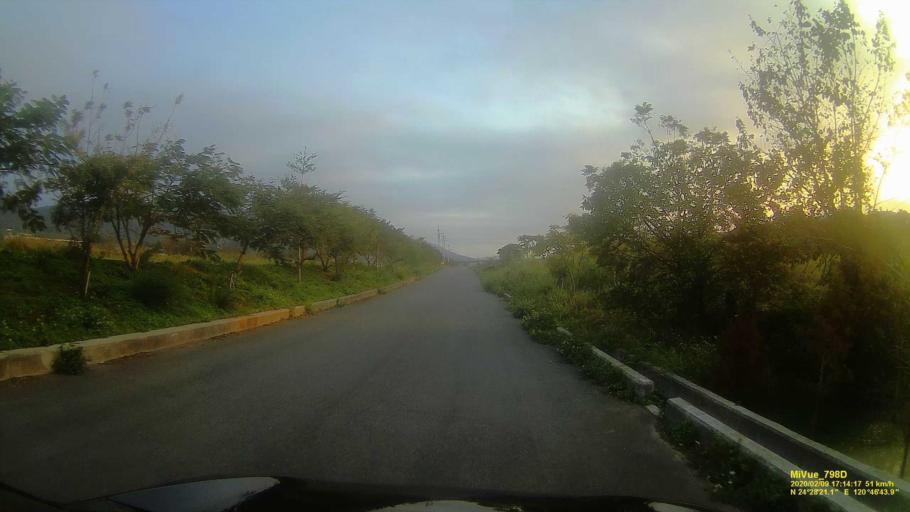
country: TW
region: Taiwan
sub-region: Miaoli
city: Miaoli
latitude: 24.4722
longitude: 120.7789
